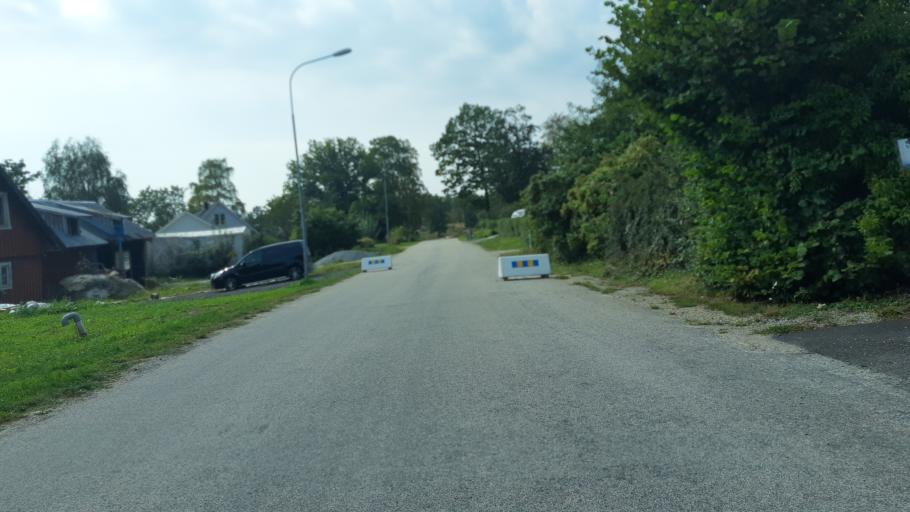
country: SE
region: Blekinge
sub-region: Karlskrona Kommun
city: Nattraby
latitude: 56.1815
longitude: 15.4975
